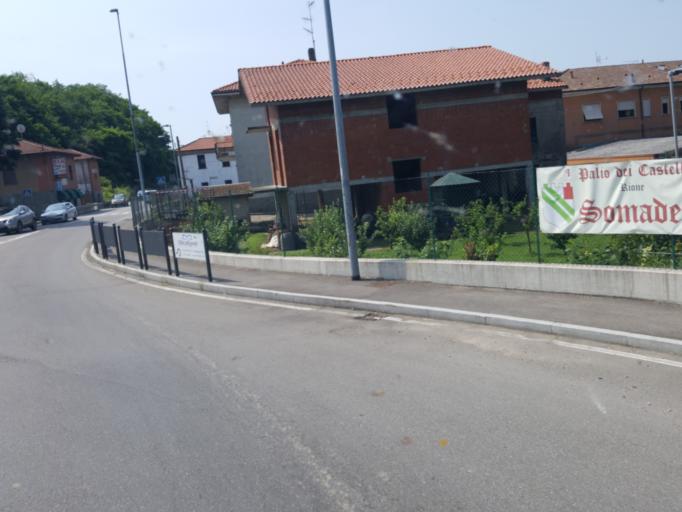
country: IT
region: Lombardy
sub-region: Provincia di Varese
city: Castiglione Olona
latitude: 45.7444
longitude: 8.8800
